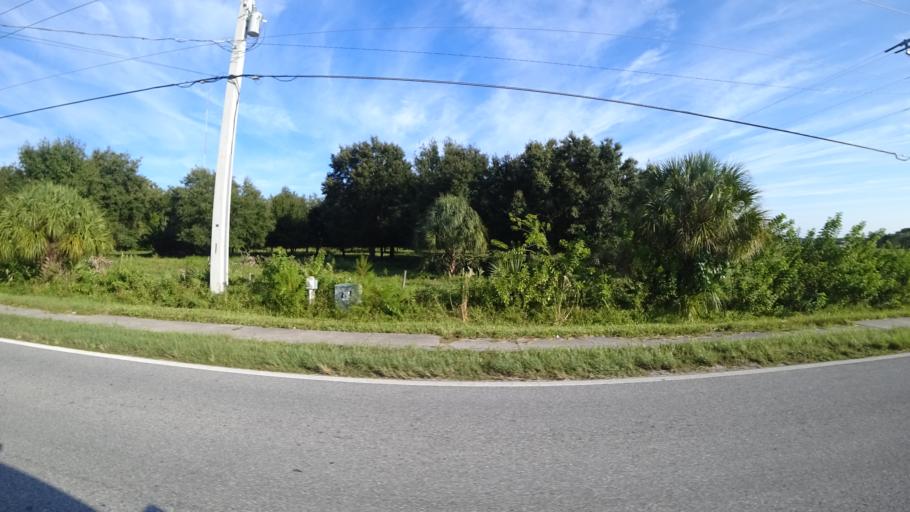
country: US
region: Florida
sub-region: Manatee County
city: Samoset
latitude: 27.4730
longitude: -82.5335
